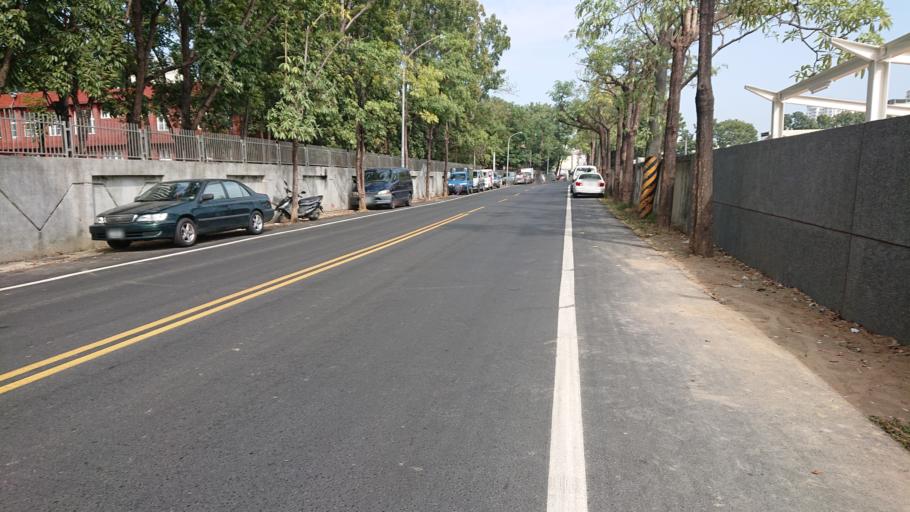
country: TW
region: Taiwan
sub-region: Tainan
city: Tainan
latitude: 23.0218
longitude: 120.2556
